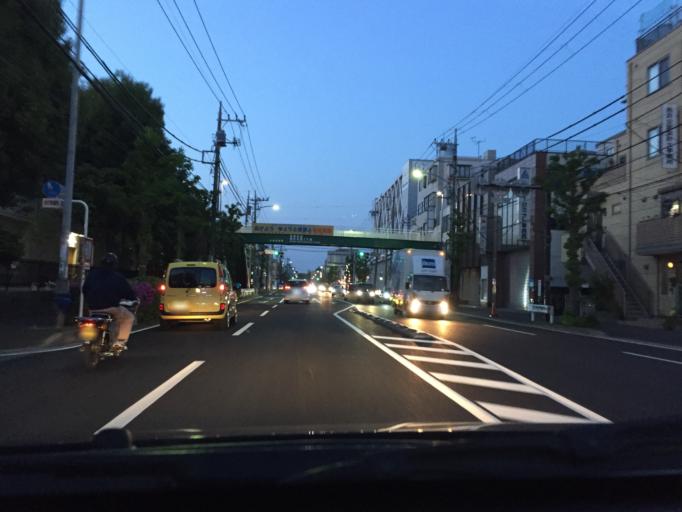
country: JP
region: Kanagawa
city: Yokohama
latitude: 35.4184
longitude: 139.5995
